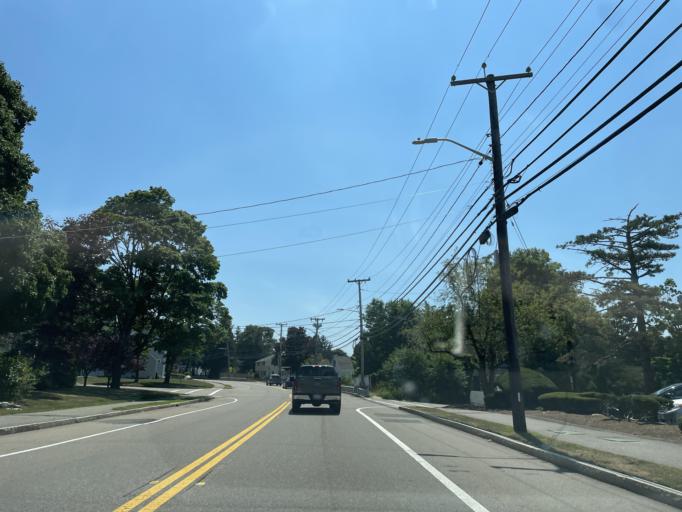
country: US
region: Massachusetts
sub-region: Norfolk County
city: Holbrook
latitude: 42.1803
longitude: -71.0145
